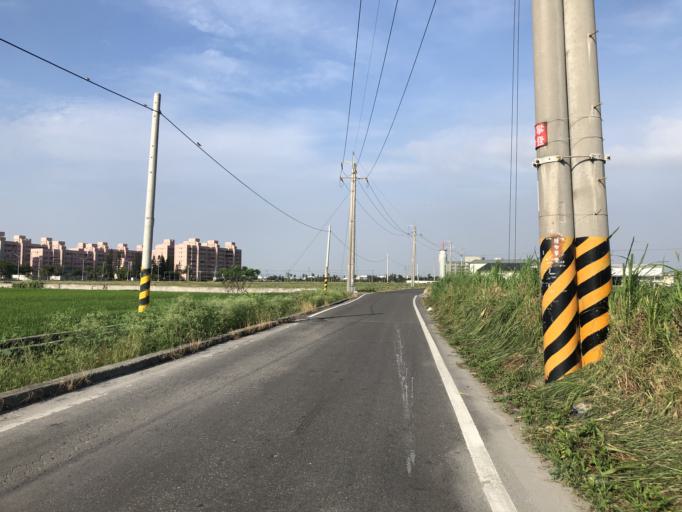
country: TW
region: Taiwan
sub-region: Changhua
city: Chang-hua
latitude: 24.0535
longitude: 120.4613
